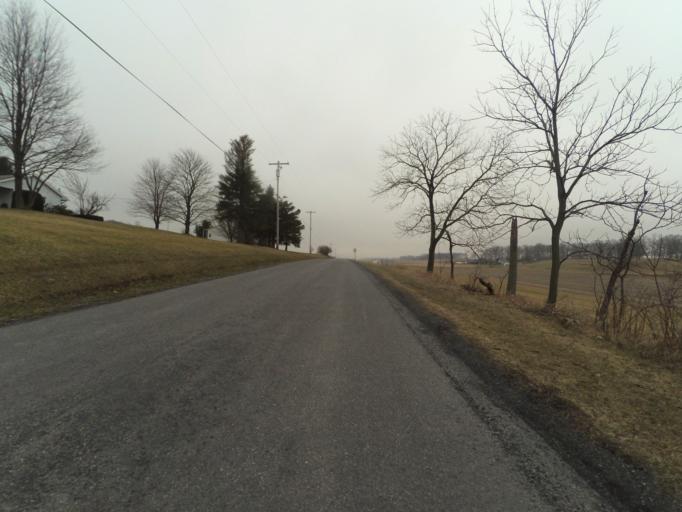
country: US
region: Pennsylvania
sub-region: Centre County
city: Centre Hall
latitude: 40.8147
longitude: -77.6536
